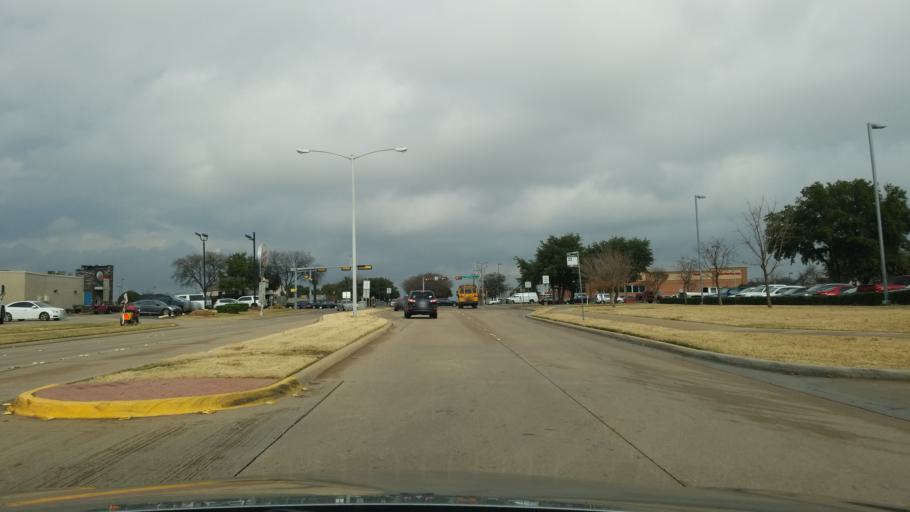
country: US
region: Texas
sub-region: Denton County
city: Lewisville
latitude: 33.0409
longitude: -97.0206
